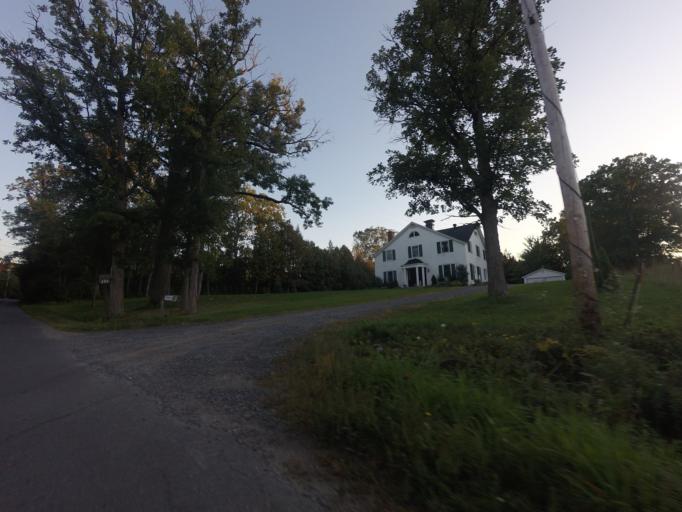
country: CA
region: Quebec
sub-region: Laurentides
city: Oka
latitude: 45.4465
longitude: -74.1080
